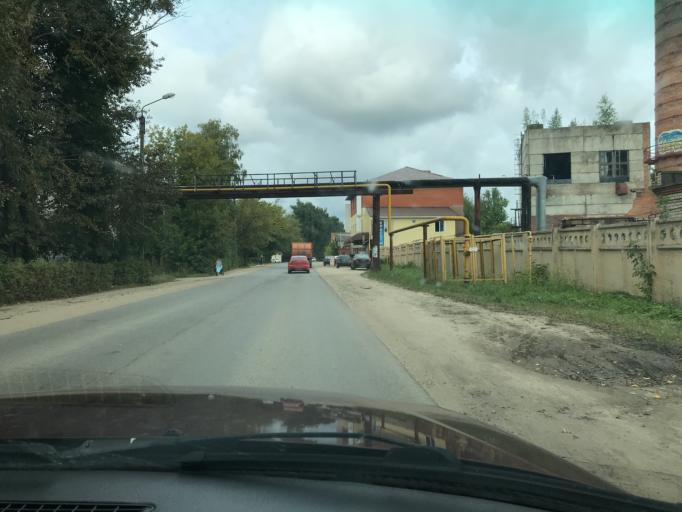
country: RU
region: Kaluga
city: Maloyaroslavets
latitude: 55.0049
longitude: 36.4726
